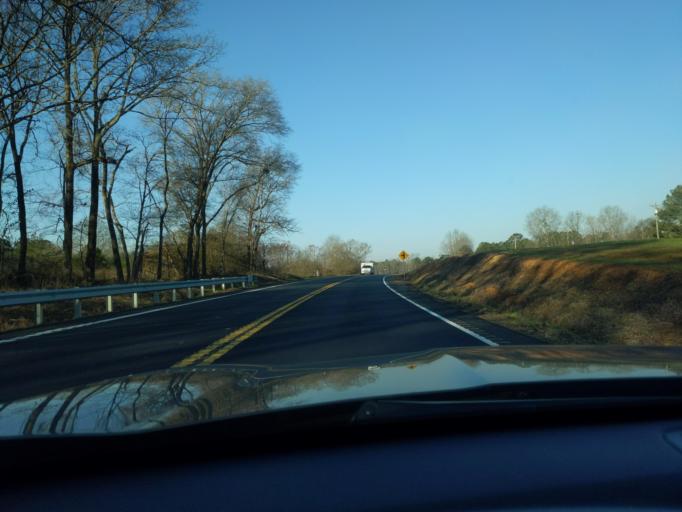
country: US
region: South Carolina
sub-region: Newberry County
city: Newberry
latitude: 34.1963
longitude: -81.7938
